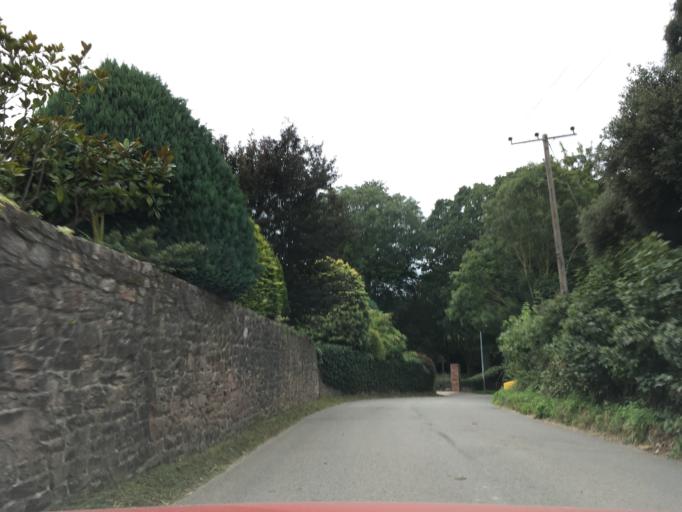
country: GB
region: Wales
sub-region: Monmouthshire
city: Chepstow
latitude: 51.6169
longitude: -2.6892
